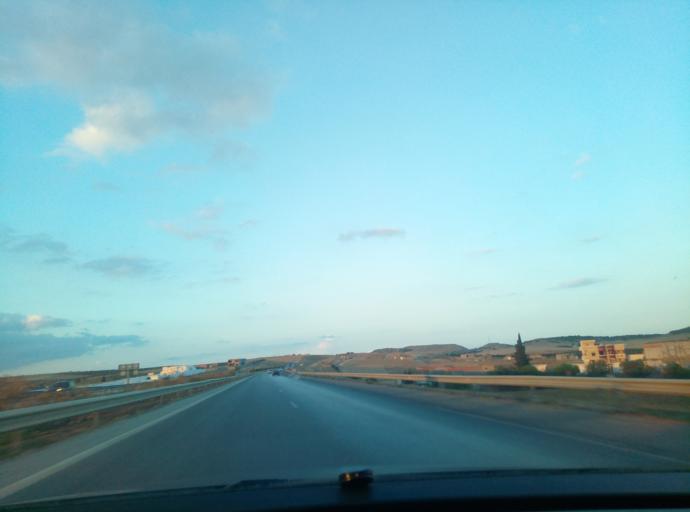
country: TN
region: Manouba
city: Manouba
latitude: 36.7474
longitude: 10.0375
